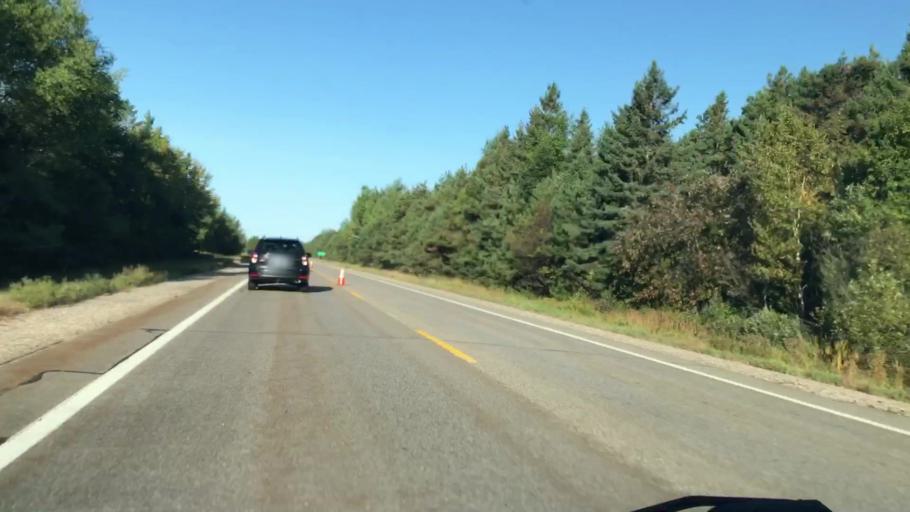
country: US
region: Michigan
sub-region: Chippewa County
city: Sault Ste. Marie
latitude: 46.3755
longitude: -84.6067
